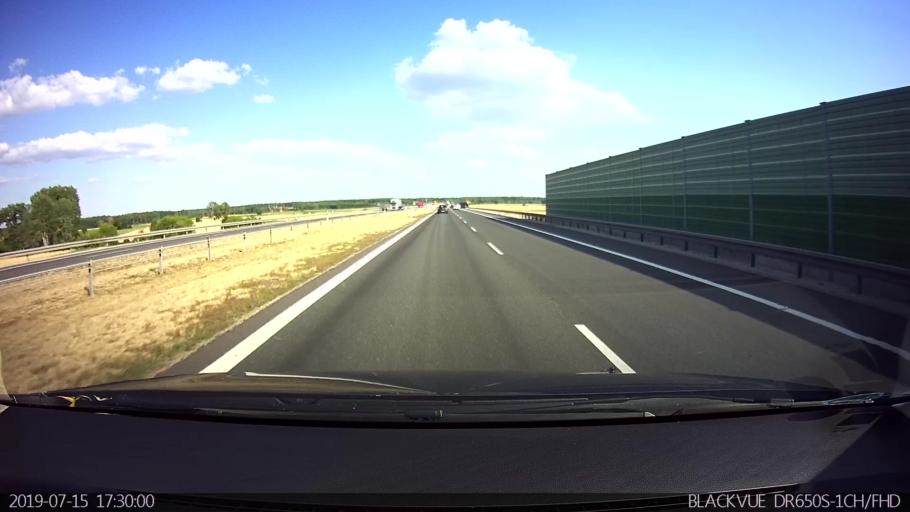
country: PL
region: Lodz Voivodeship
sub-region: Powiat wieruszowski
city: Wieruszow
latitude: 51.3237
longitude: 18.1569
